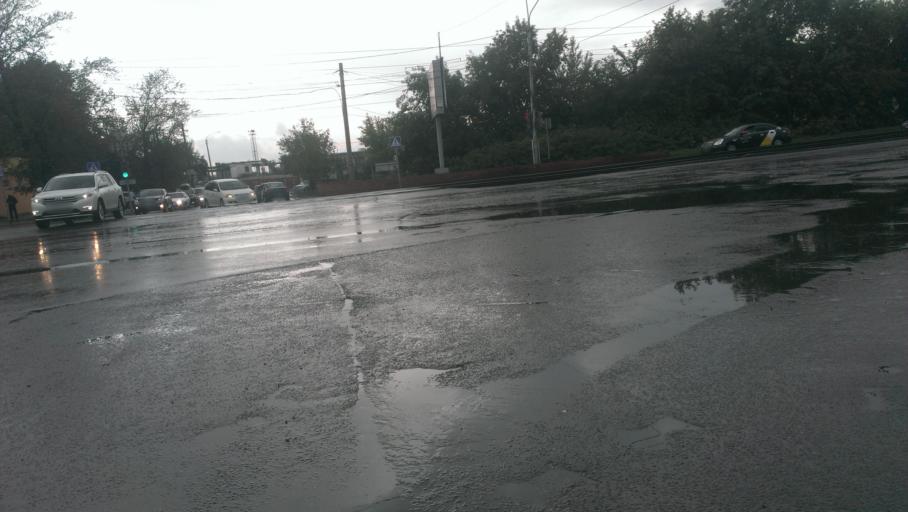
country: RU
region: Altai Krai
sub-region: Gorod Barnaulskiy
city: Barnaul
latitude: 53.3612
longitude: 83.7634
